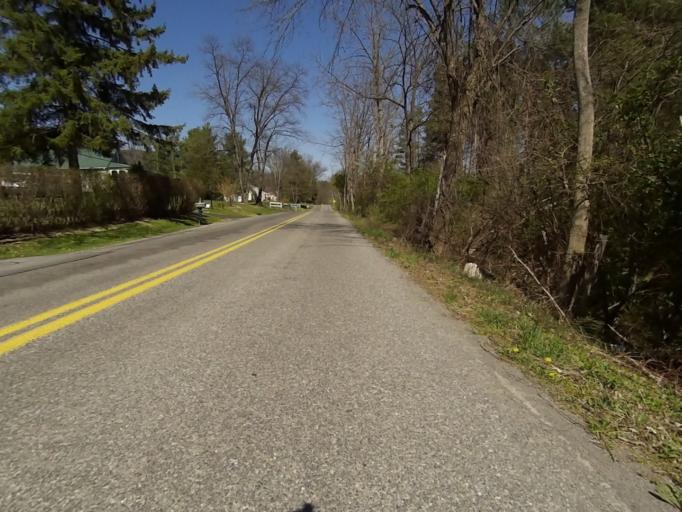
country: US
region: Pennsylvania
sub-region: Centre County
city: Houserville
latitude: 40.8800
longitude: -77.8685
